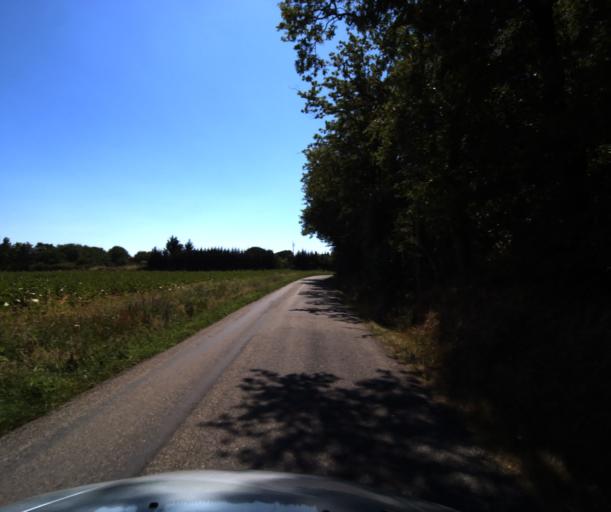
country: FR
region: Midi-Pyrenees
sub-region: Departement de la Haute-Garonne
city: Muret
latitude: 43.4523
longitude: 1.3533
